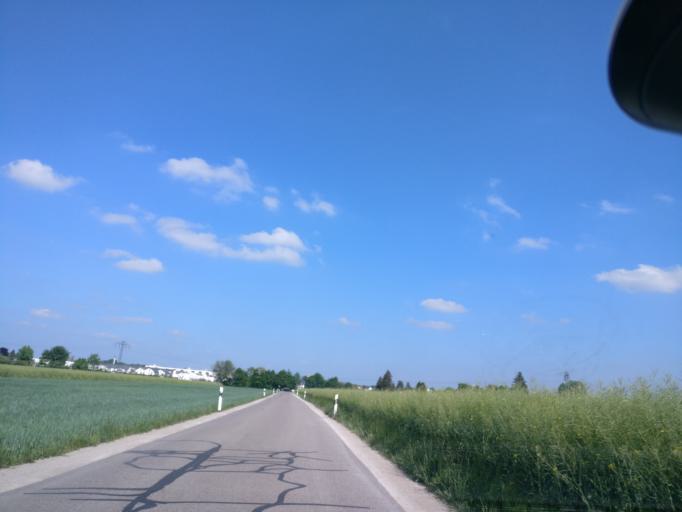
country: DE
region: Bavaria
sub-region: Upper Bavaria
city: Karlsfeld
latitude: 48.2121
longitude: 11.4424
